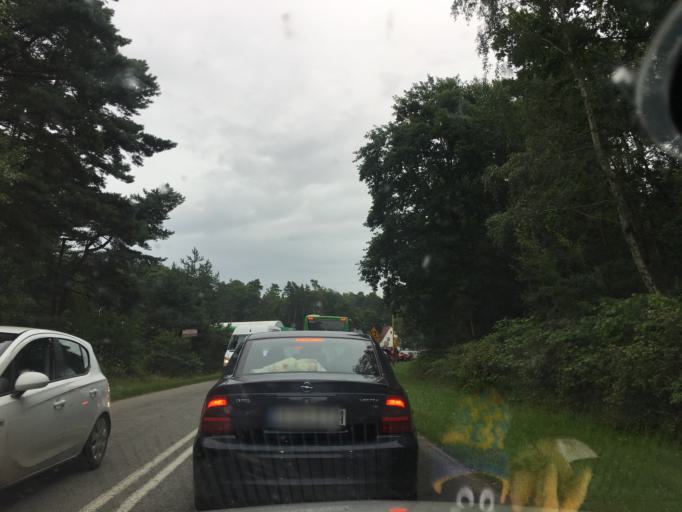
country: PL
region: West Pomeranian Voivodeship
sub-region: Powiat gryficki
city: Pobierowo
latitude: 54.0546
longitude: 14.9389
